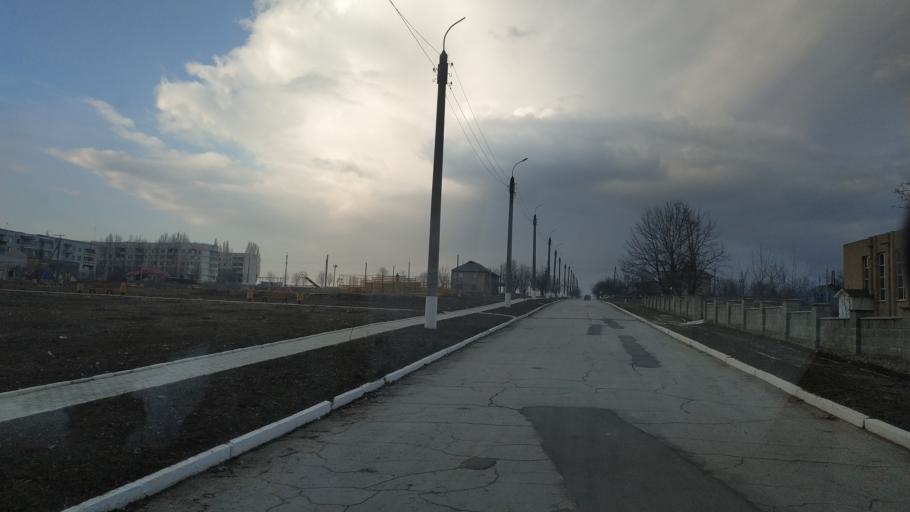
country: MD
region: Telenesti
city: Grigoriopol
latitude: 47.0100
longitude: 29.2948
